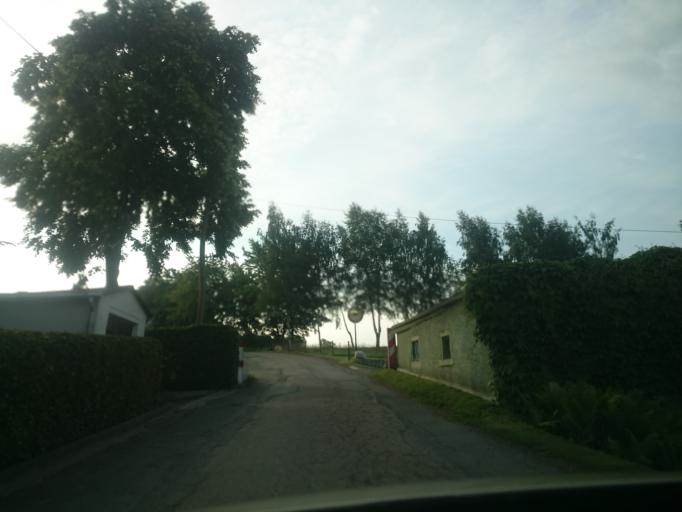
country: DE
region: Saxony
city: Eppendorf
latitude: 50.8354
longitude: 13.2255
